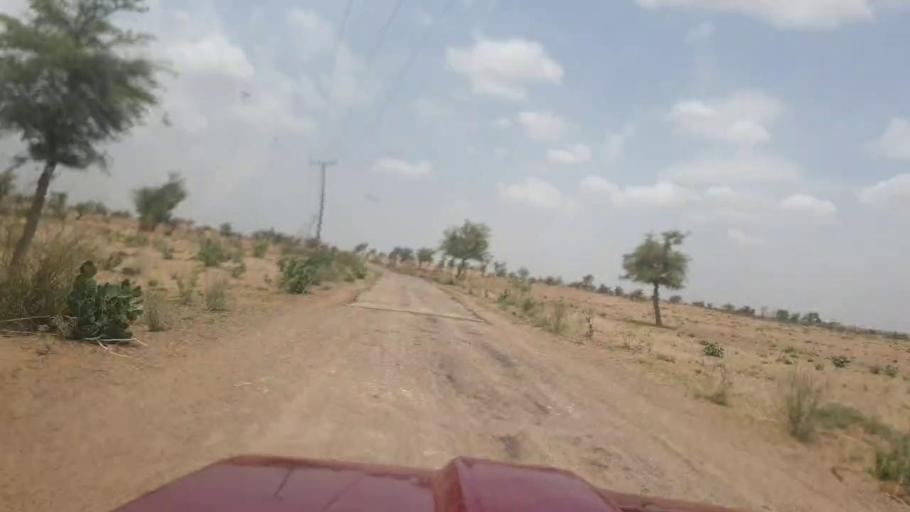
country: PK
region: Sindh
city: Islamkot
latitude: 25.2231
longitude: 70.4767
